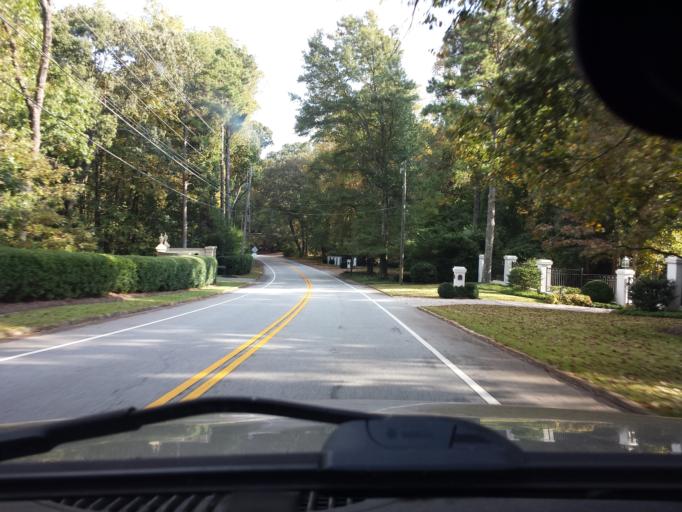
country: US
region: Georgia
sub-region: Cobb County
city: Vinings
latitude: 33.8932
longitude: -84.4300
